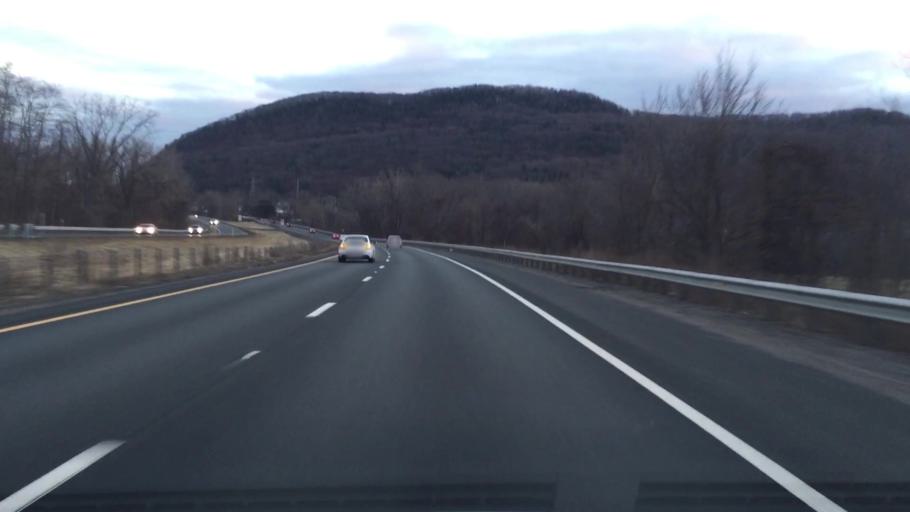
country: US
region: Massachusetts
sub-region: Hampshire County
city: Northampton
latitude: 42.2913
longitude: -72.6276
